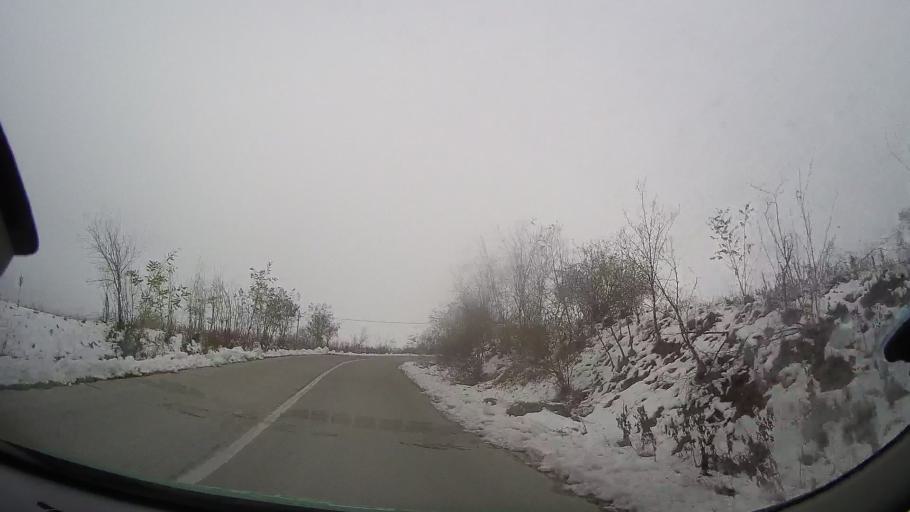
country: RO
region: Bacau
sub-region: Comuna Podu Turcului
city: Podu Turcului
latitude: 46.2032
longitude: 27.3940
